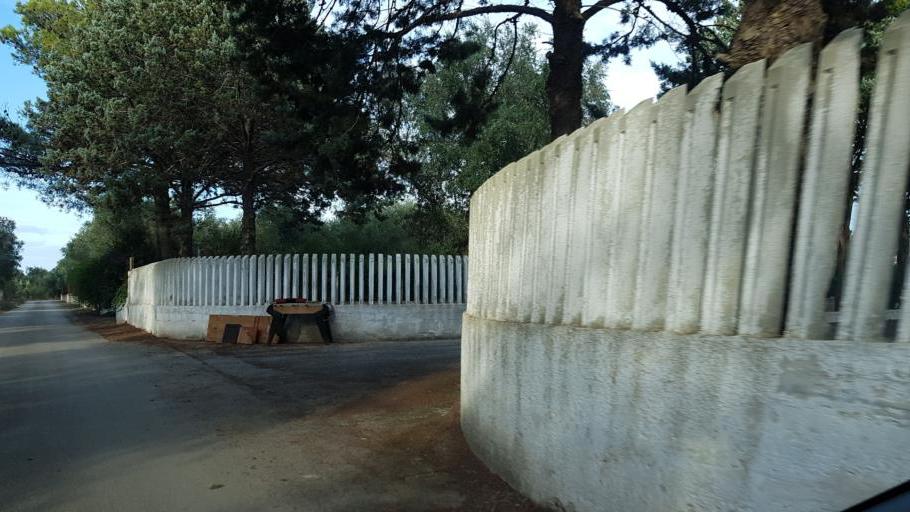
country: IT
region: Apulia
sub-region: Provincia di Brindisi
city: Oria
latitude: 40.5018
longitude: 17.6709
